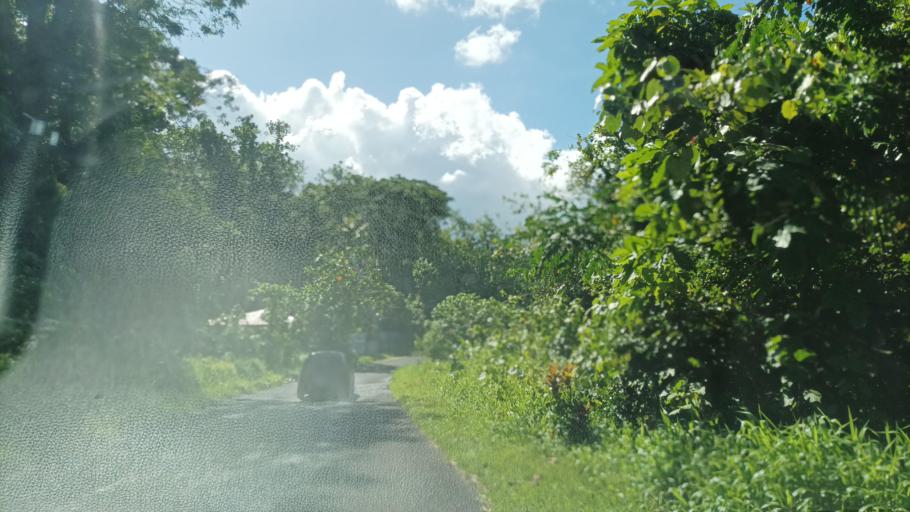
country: FM
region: Pohnpei
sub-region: Madolenihm Municipality
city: Madolenihm Municipality Government
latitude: 6.8631
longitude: 158.2927
